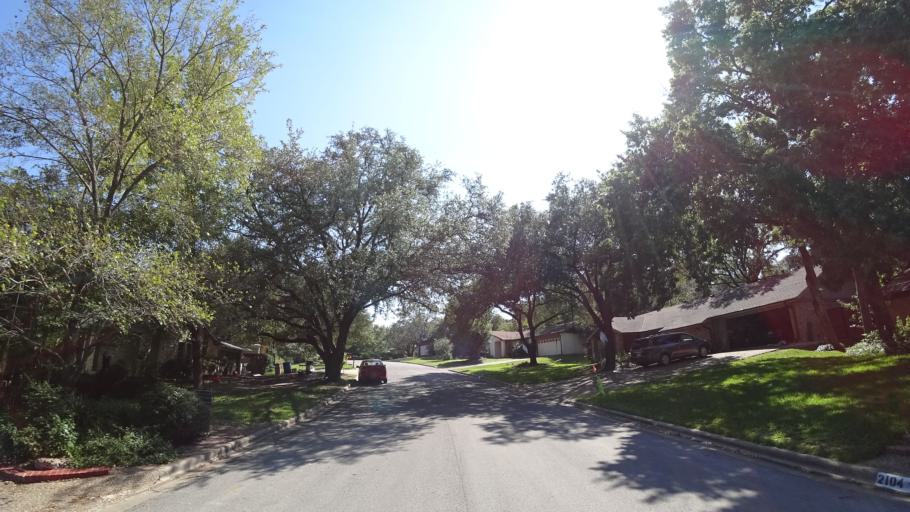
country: US
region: Texas
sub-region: Travis County
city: Rollingwood
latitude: 30.2526
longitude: -97.7890
